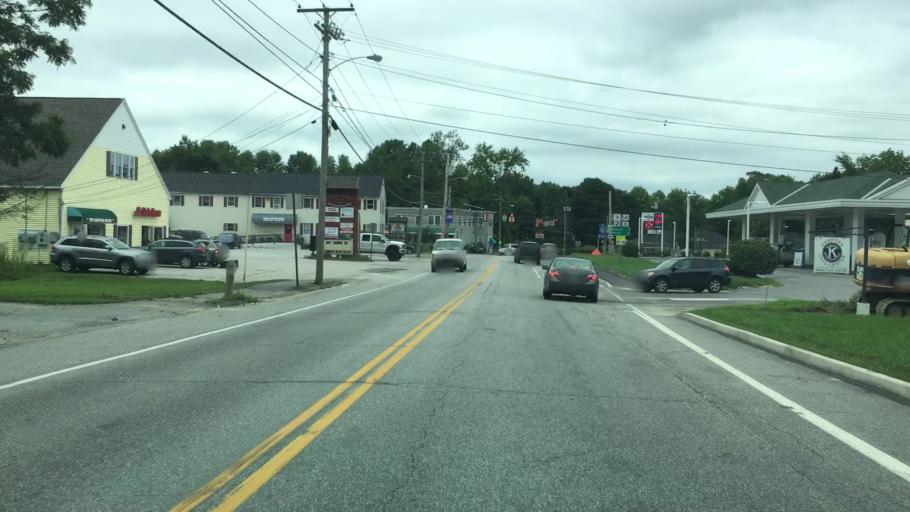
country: US
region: Maine
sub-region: Penobscot County
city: Hampden
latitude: 44.7435
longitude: -68.8379
